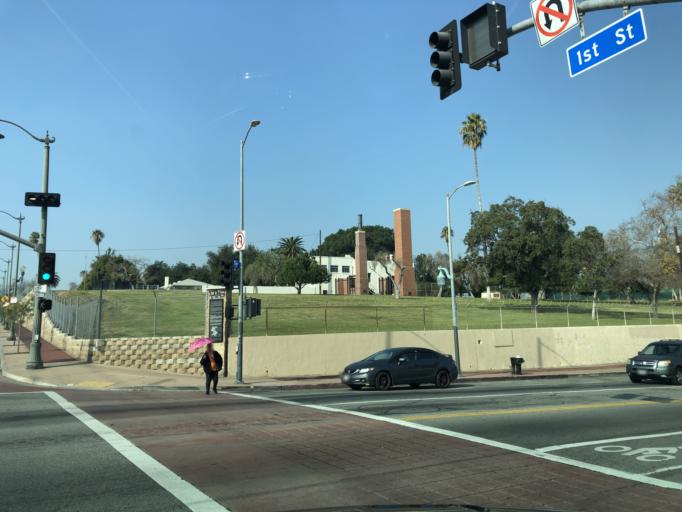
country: US
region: California
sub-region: Los Angeles County
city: Boyle Heights
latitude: 34.0372
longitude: -118.1949
